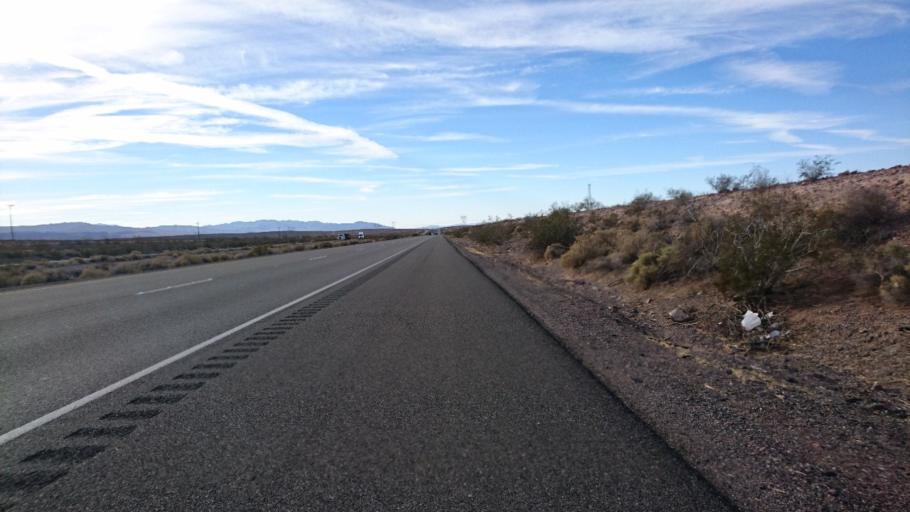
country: US
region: California
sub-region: San Bernardino County
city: Fort Irwin
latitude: 34.7751
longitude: -116.3780
